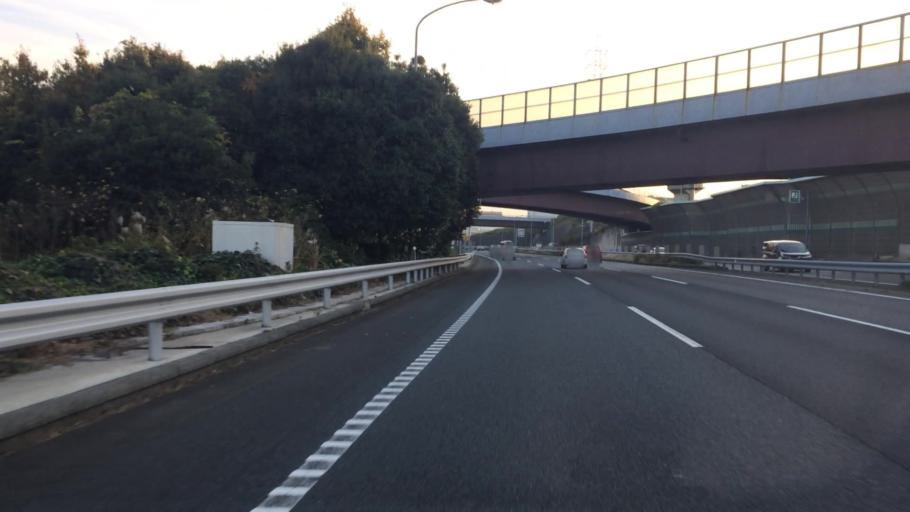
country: JP
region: Kanagawa
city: Yokohama
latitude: 35.5471
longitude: 139.6029
